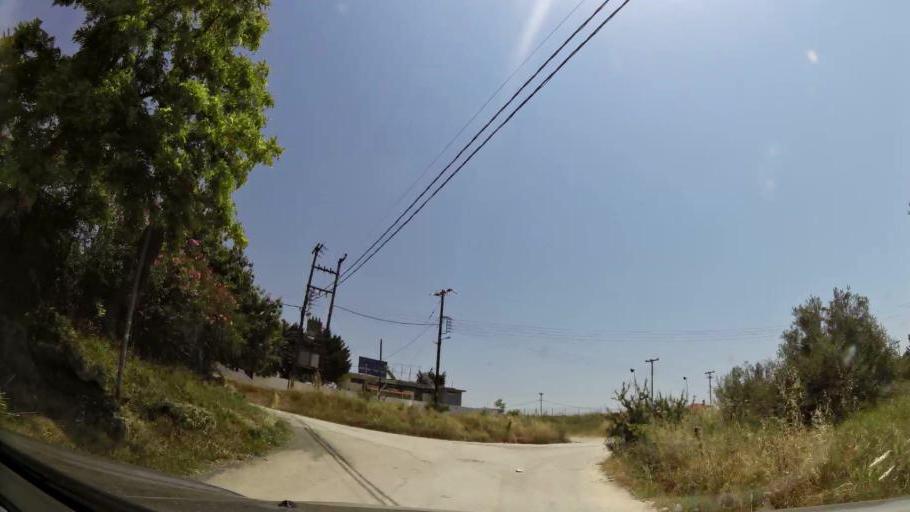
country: GR
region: Central Macedonia
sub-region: Nomos Thessalonikis
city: Epanomi
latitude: 40.4248
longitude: 22.9354
